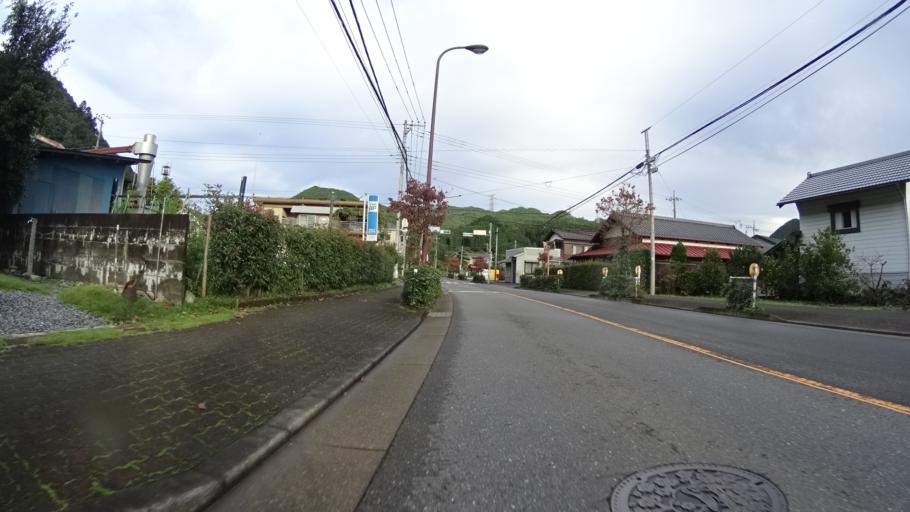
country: JP
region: Tokyo
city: Ome
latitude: 35.8016
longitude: 139.2102
